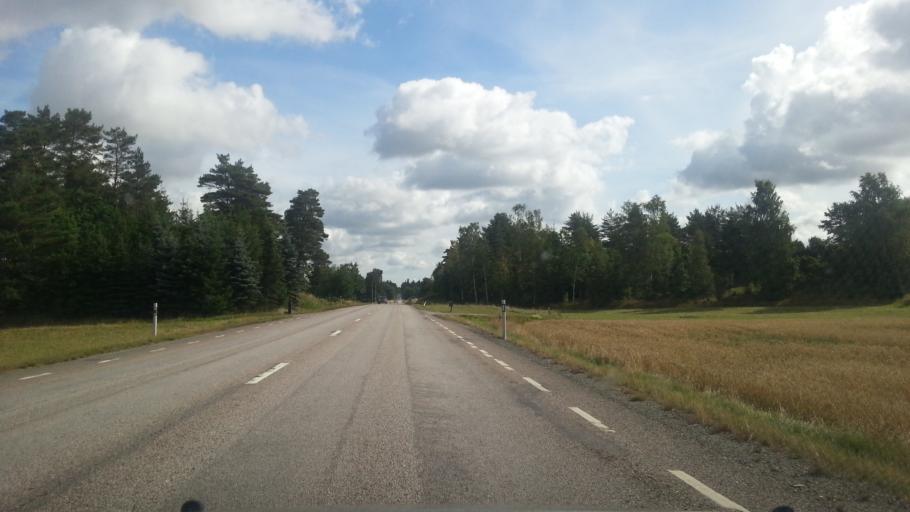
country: SE
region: Vaestra Goetaland
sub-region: Vara Kommun
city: Vara
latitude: 58.4199
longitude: 12.8692
